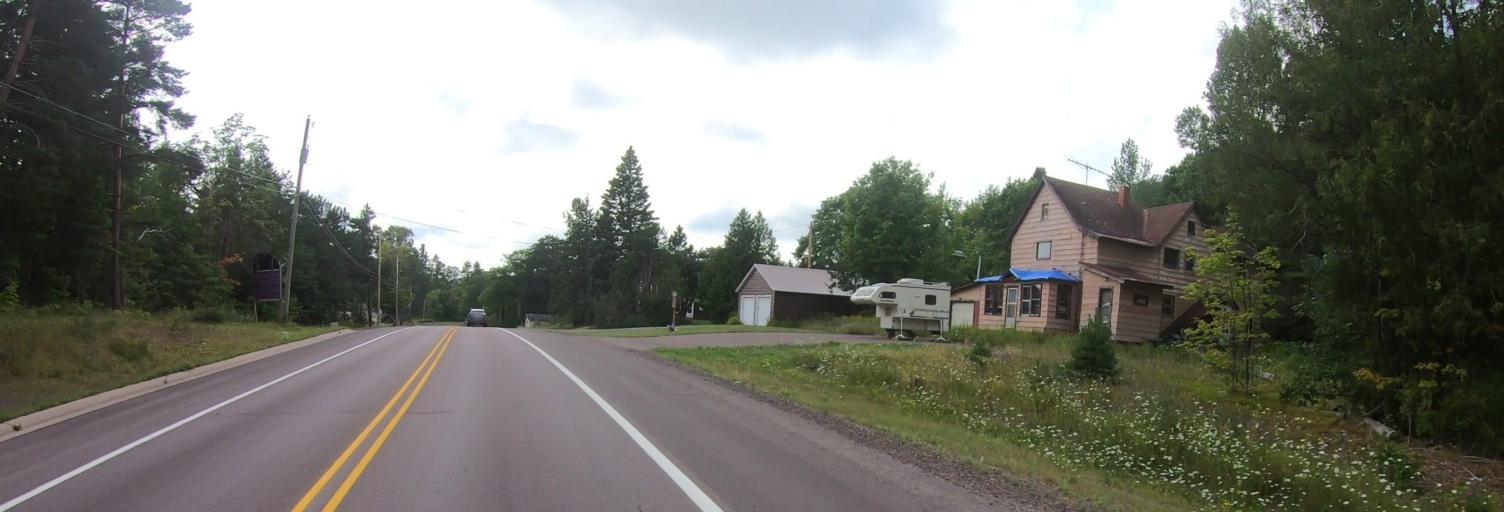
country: US
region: Michigan
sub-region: Houghton County
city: Hancock
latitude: 47.0591
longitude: -88.6591
